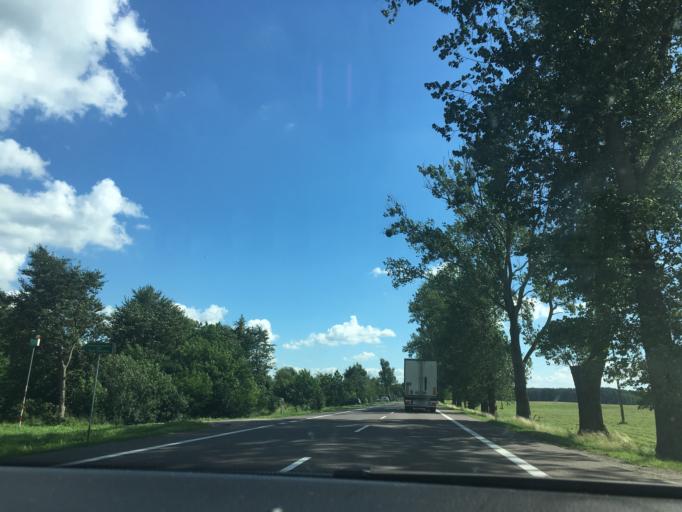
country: PL
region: Podlasie
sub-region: Powiat augustowski
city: Augustow
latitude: 53.8219
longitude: 22.9627
